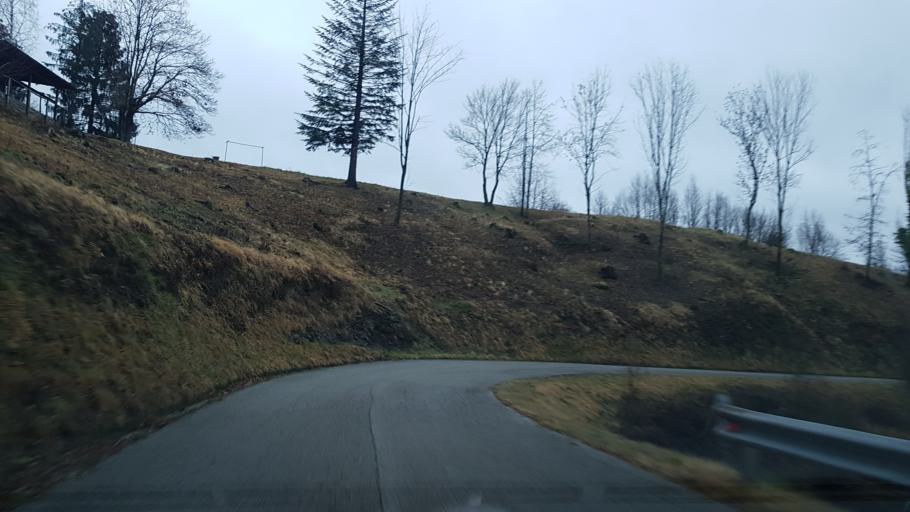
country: IT
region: Friuli Venezia Giulia
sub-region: Provincia di Udine
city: Stregna
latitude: 46.1214
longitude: 13.5985
